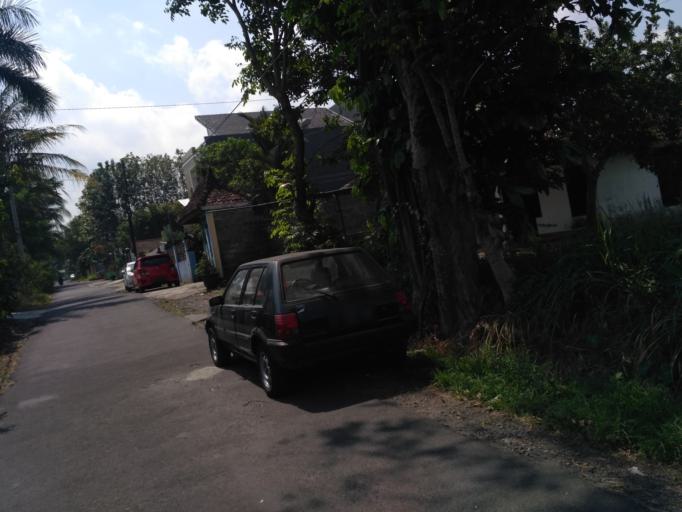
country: ID
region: Daerah Istimewa Yogyakarta
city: Melati
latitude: -7.7081
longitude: 110.4158
